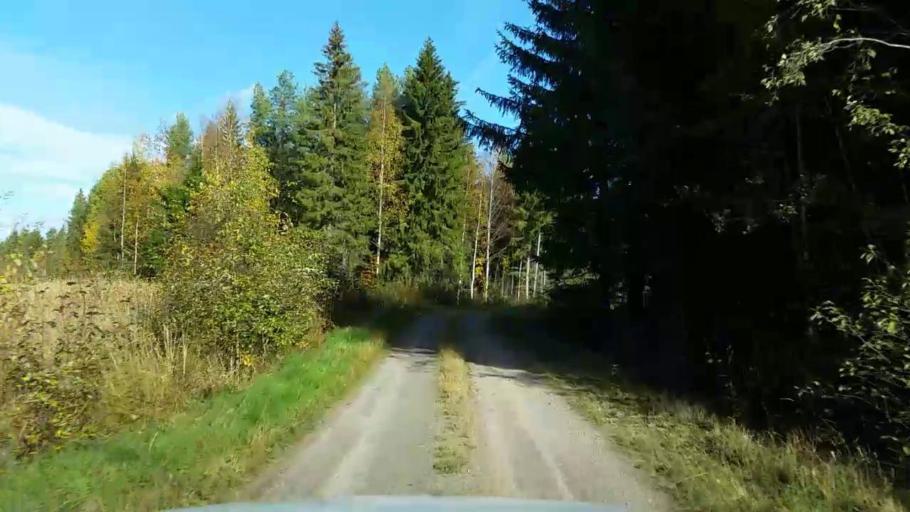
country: SE
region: Gaevleborg
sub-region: Ljusdals Kommun
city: Jaervsoe
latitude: 61.7887
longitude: 16.1565
